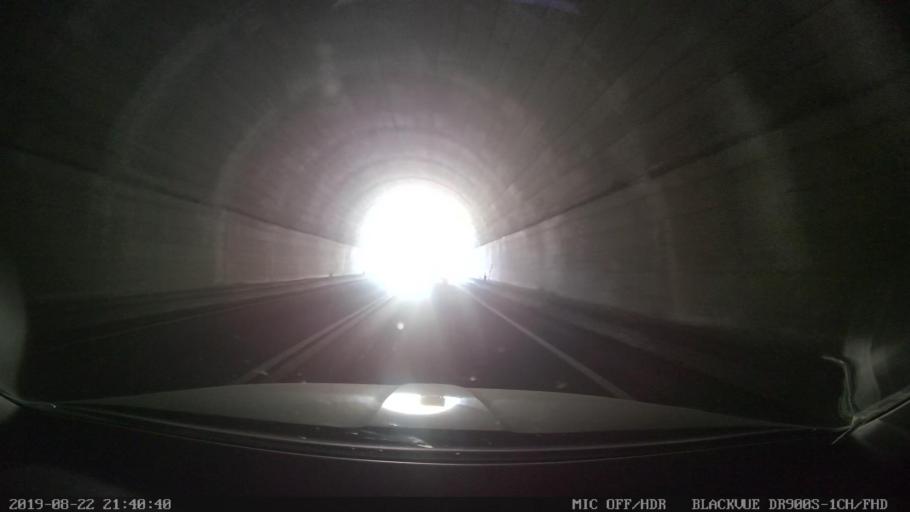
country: PT
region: Leiria
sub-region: Figueiro Dos Vinhos
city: Figueiro dos Vinhos
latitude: 39.9276
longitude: -8.3129
